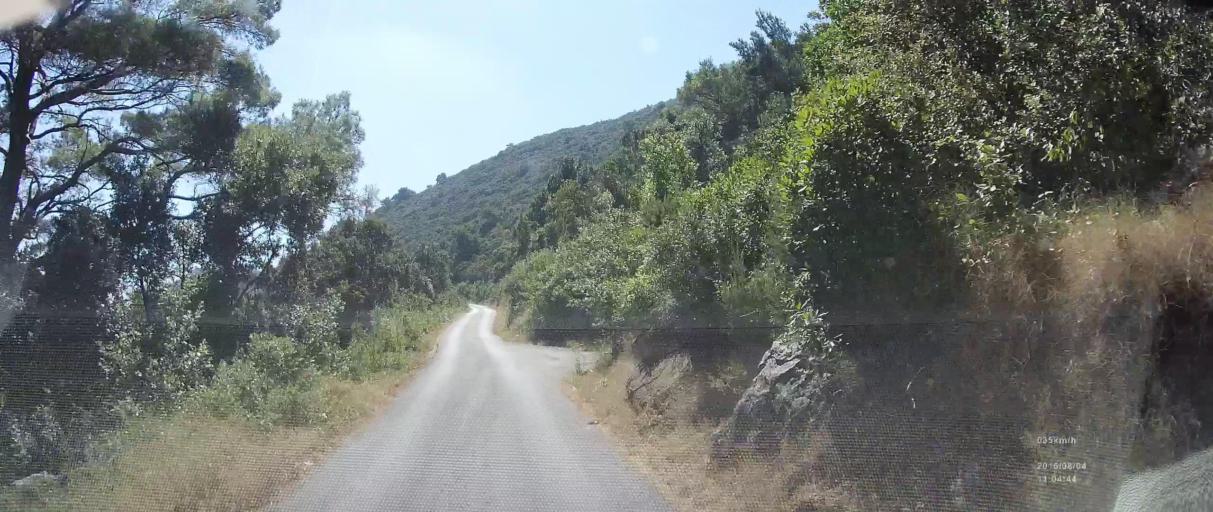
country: HR
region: Dubrovacko-Neretvanska
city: Blato
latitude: 42.7772
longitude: 17.4542
